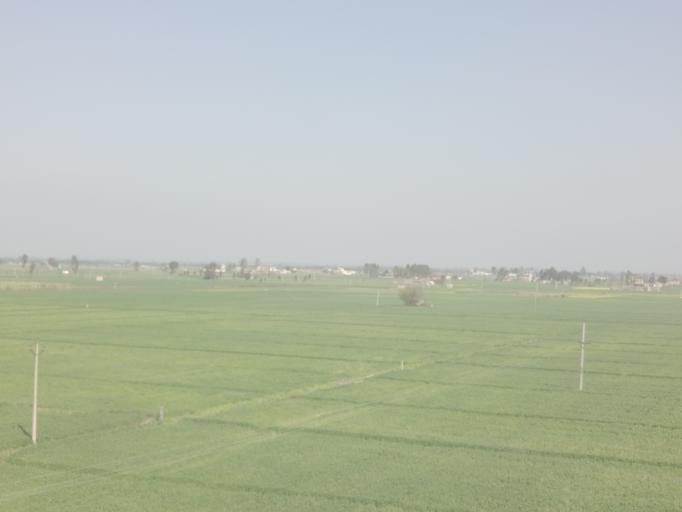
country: IN
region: Punjab
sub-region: Shahid Bhagat Singh Nagar
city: Rahon
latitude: 31.0221
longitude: 76.0926
